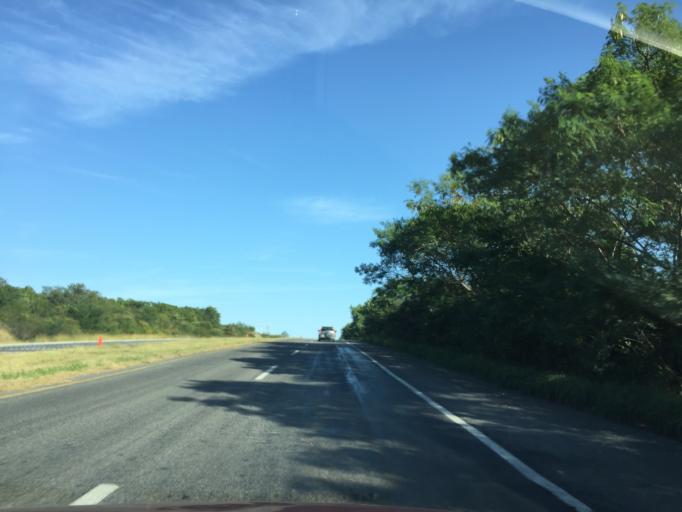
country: MX
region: Nuevo Leon
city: Montemorelos
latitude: 25.1321
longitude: -99.8242
